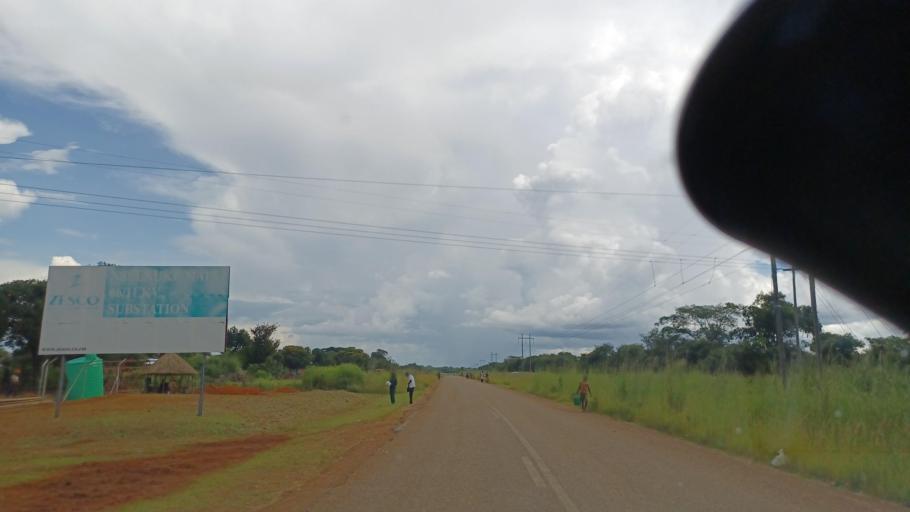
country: ZM
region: North-Western
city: Kasempa
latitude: -13.1127
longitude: 25.8696
